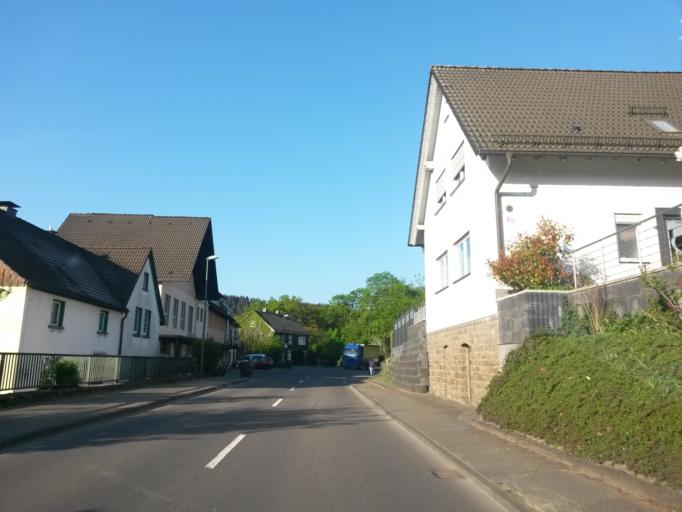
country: DE
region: North Rhine-Westphalia
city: Wiehl
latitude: 50.9610
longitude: 7.5163
